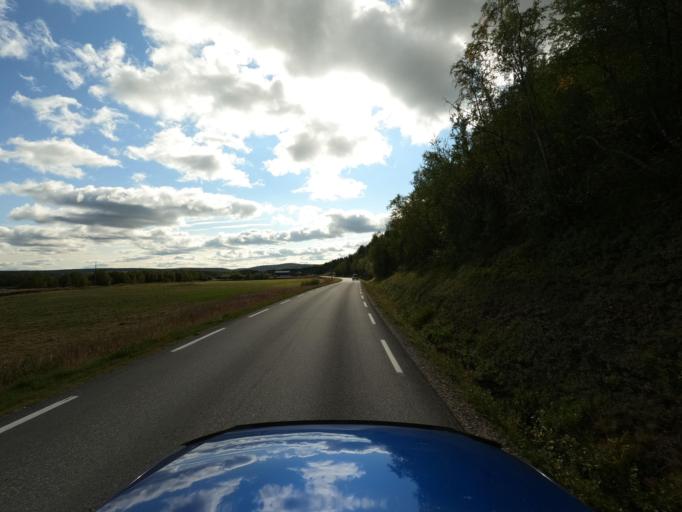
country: NO
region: Finnmark Fylke
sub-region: Karasjok
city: Karasjohka
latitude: 69.4095
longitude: 25.8061
